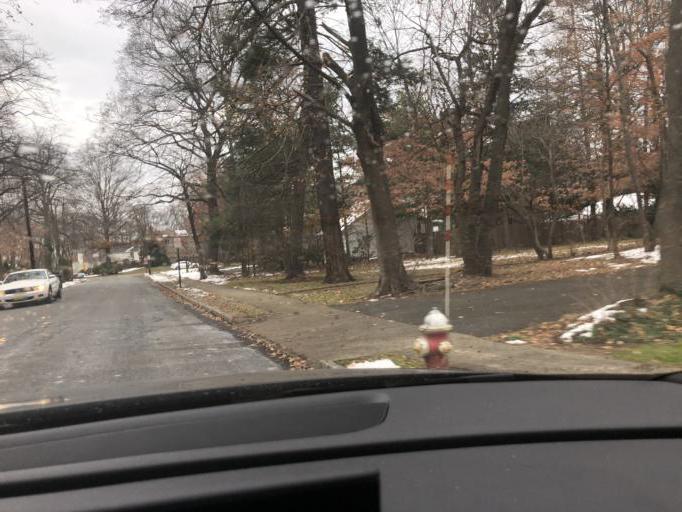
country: US
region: New Jersey
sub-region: Morris County
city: Morristown
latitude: 40.7954
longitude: -74.4618
